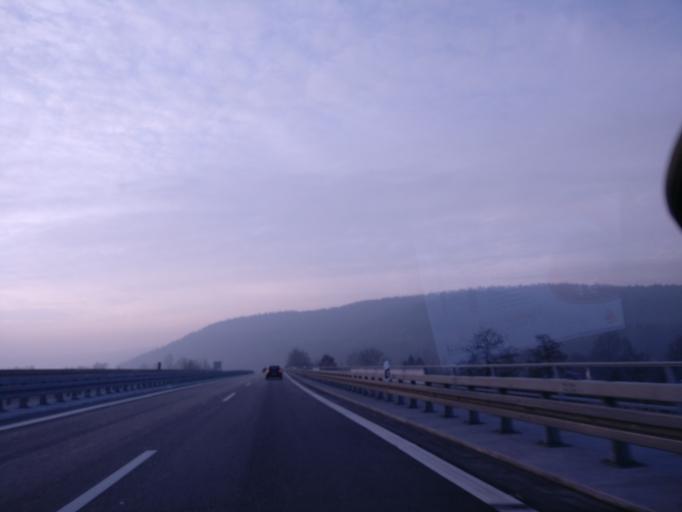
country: DE
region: Baden-Wuerttemberg
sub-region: Regierungsbezirk Stuttgart
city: Urbach
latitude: 48.8069
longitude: 9.5714
